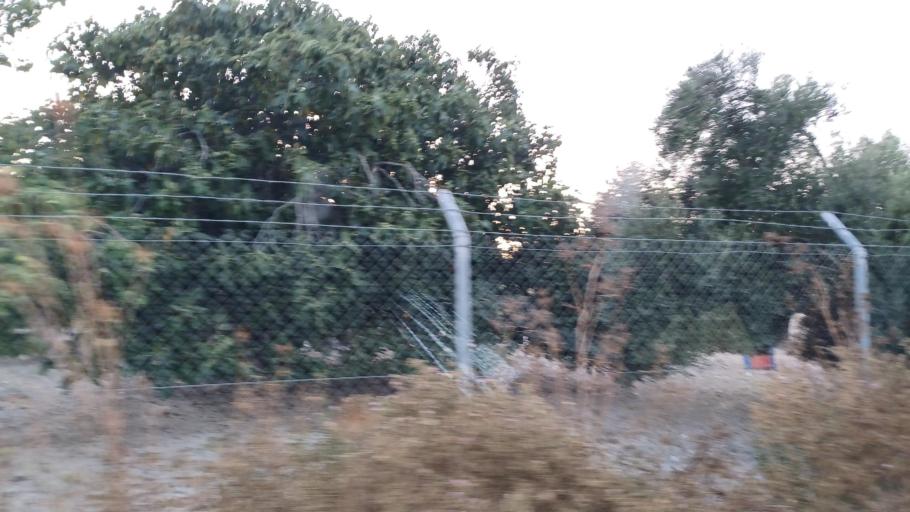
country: CY
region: Pafos
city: Tala
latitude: 34.8832
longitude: 32.4967
